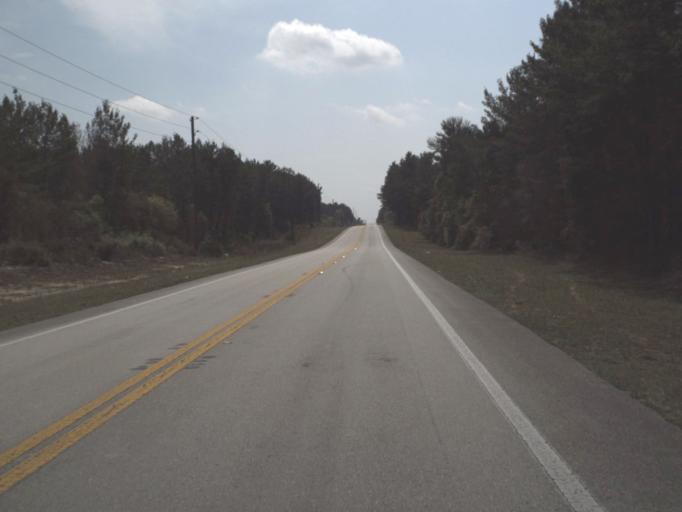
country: US
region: Florida
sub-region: Putnam County
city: Crescent City
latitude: 29.3223
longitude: -81.7013
